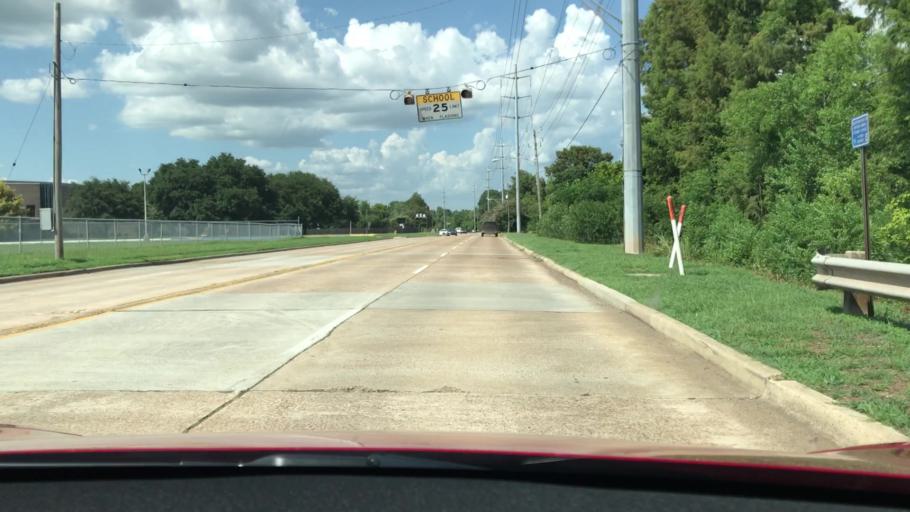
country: US
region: Louisiana
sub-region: Bossier Parish
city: Bossier City
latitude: 32.4461
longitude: -93.7123
